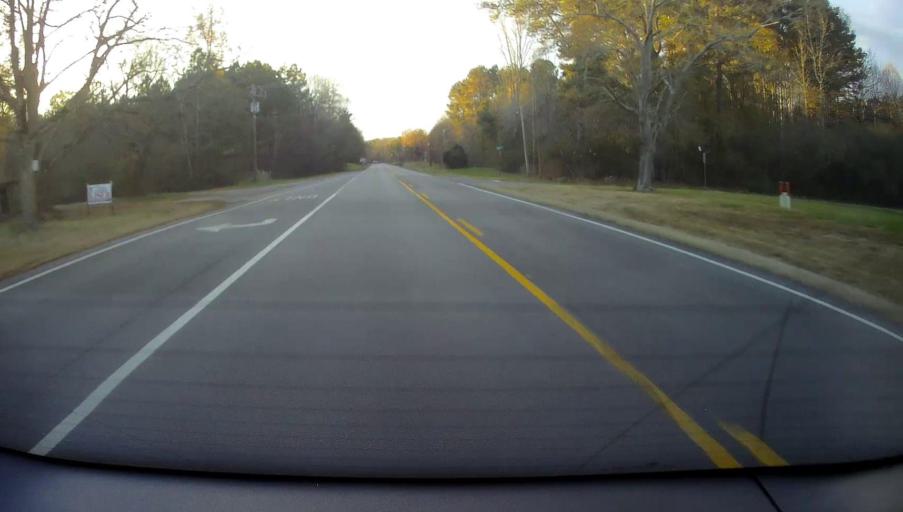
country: US
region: Alabama
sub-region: Saint Clair County
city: Steele
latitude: 34.0580
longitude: -86.2219
